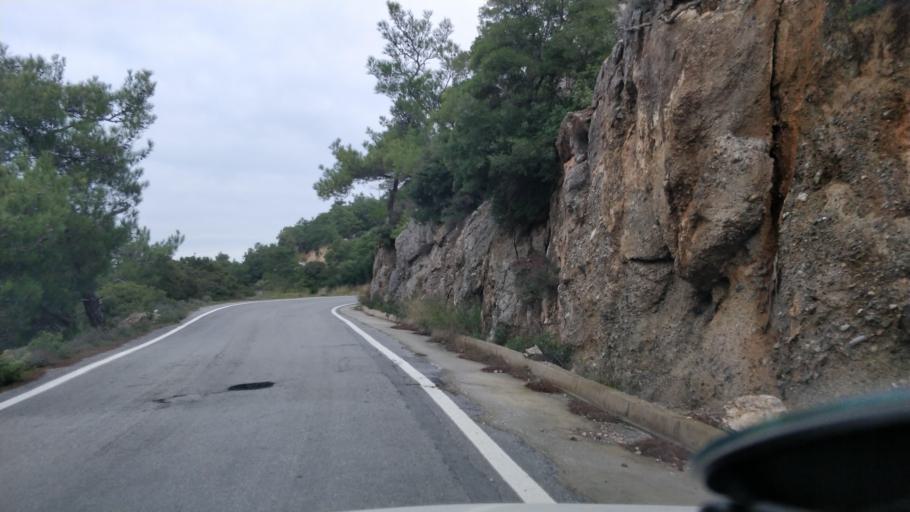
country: GR
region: Crete
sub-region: Nomos Lasithiou
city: Kritsa
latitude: 35.0979
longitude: 25.6983
